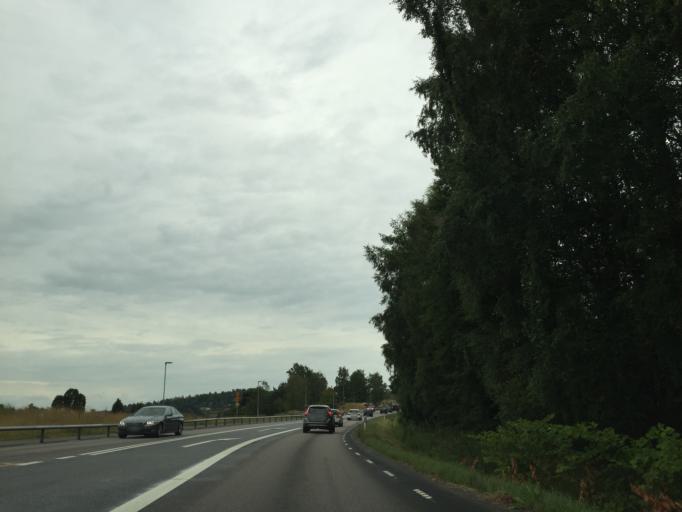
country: SE
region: Vaestra Goetaland
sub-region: Tjorns Kommun
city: Myggenas
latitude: 58.0569
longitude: 11.7597
